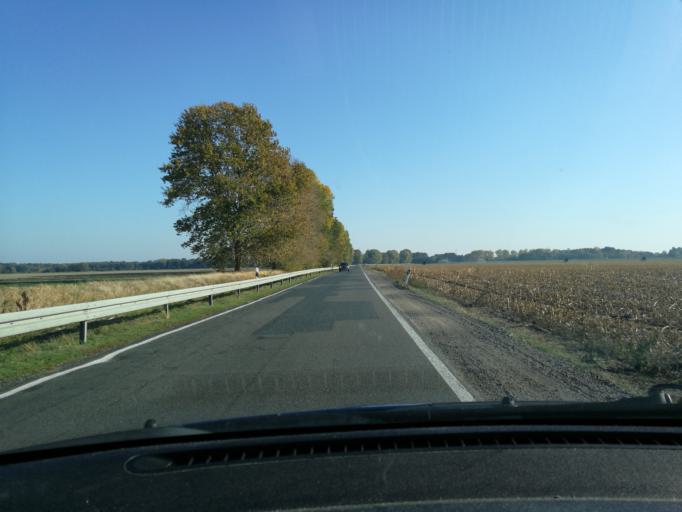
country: DE
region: Mecklenburg-Vorpommern
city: Domitz
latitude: 53.1561
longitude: 11.2464
